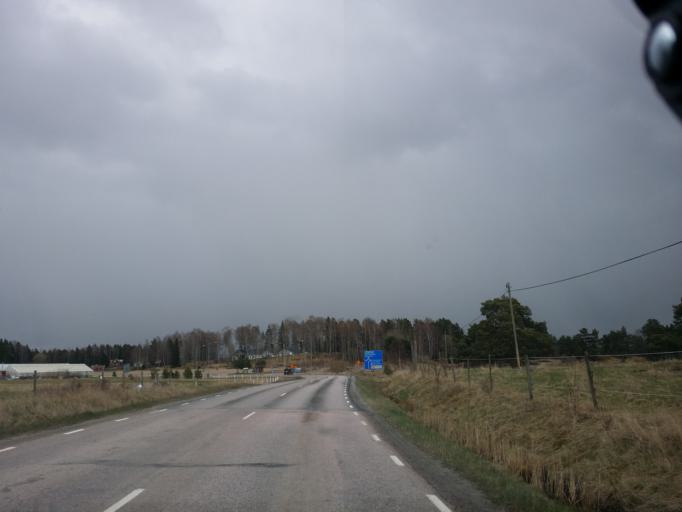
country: SE
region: Uppsala
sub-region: Enkopings Kommun
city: Enkoping
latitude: 59.6197
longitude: 17.1156
